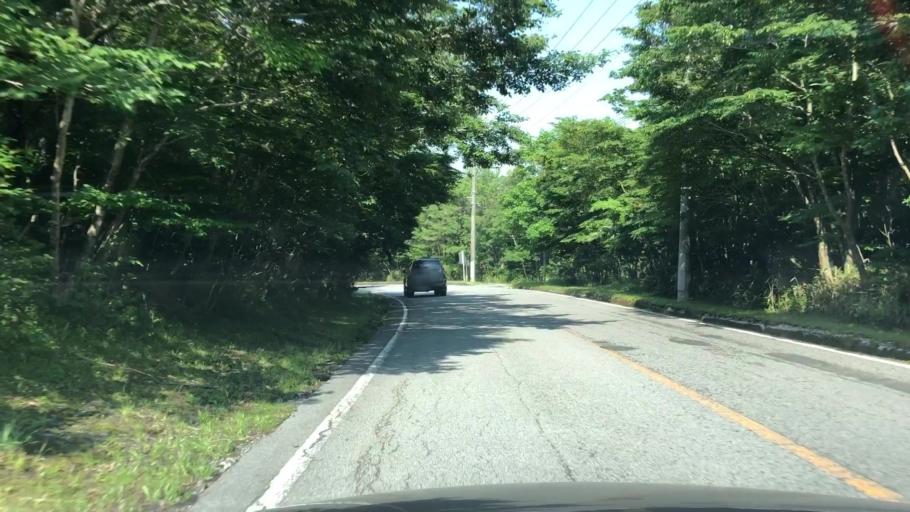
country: JP
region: Shizuoka
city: Gotemba
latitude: 35.3315
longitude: 138.8146
